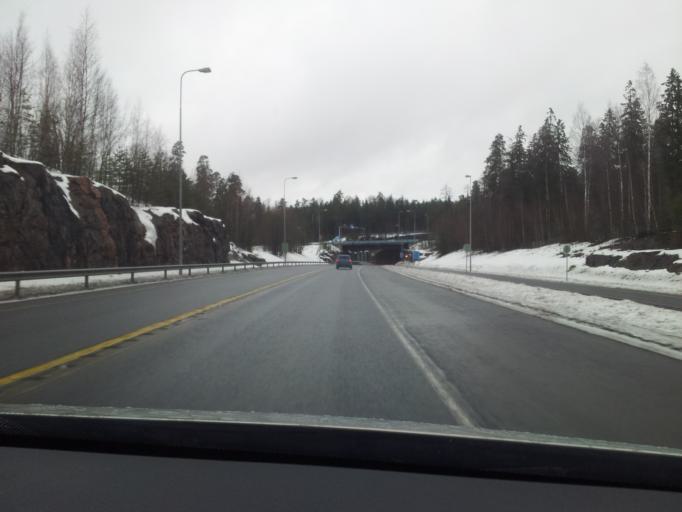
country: FI
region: Uusimaa
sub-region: Helsinki
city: Kauniainen
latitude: 60.2068
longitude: 24.7457
